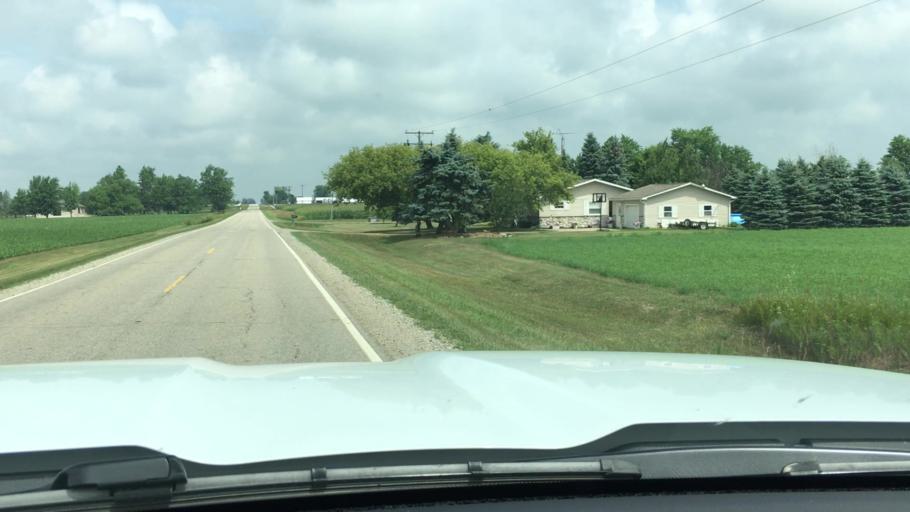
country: US
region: Michigan
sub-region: Sanilac County
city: Marlette
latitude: 43.4042
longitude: -83.0079
